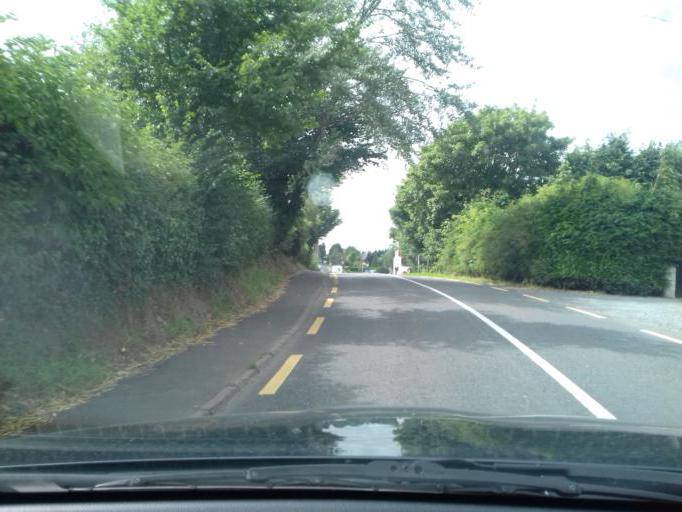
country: IE
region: Leinster
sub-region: Wicklow
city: Baltinglass
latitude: 52.8854
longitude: -6.7008
